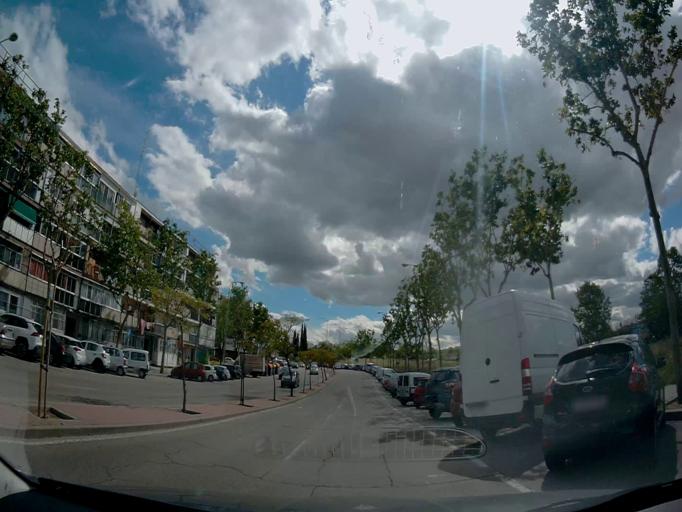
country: ES
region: Madrid
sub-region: Provincia de Madrid
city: Vicalvaro
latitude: 40.4071
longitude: -3.6162
